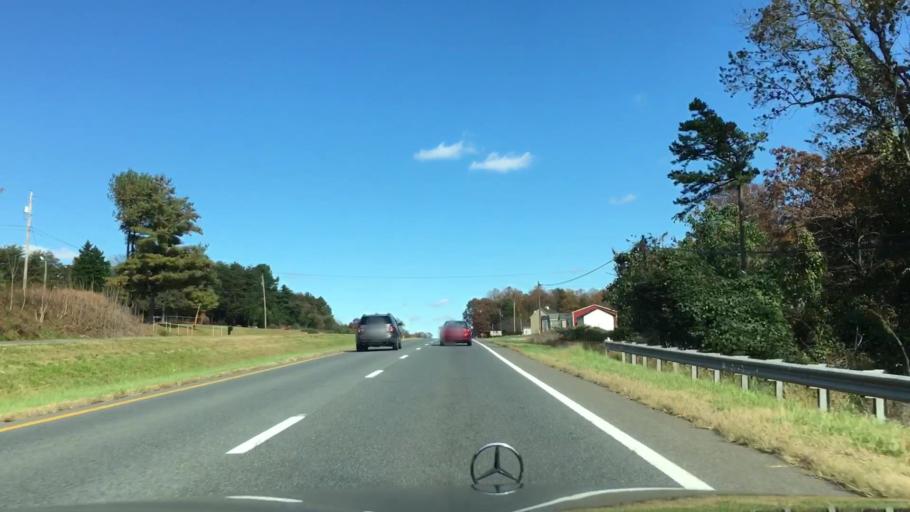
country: US
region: Virginia
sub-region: Campbell County
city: Rustburg
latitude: 37.2642
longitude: -79.1790
